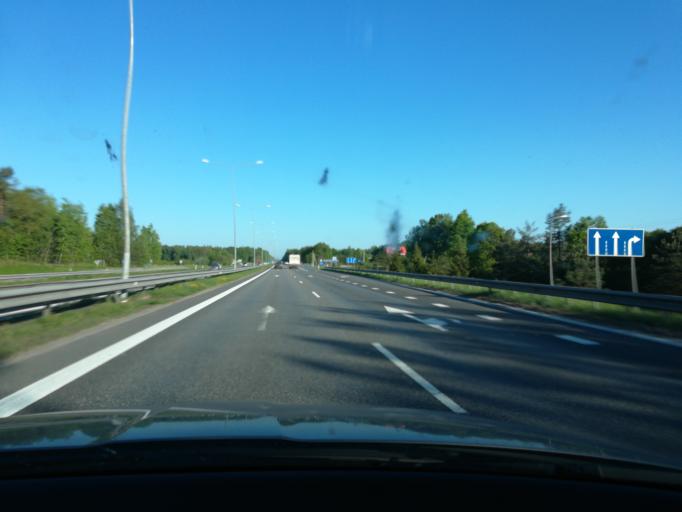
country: LT
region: Kauno apskritis
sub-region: Kauno rajonas
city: Karmelava
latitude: 54.8957
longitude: 24.1504
